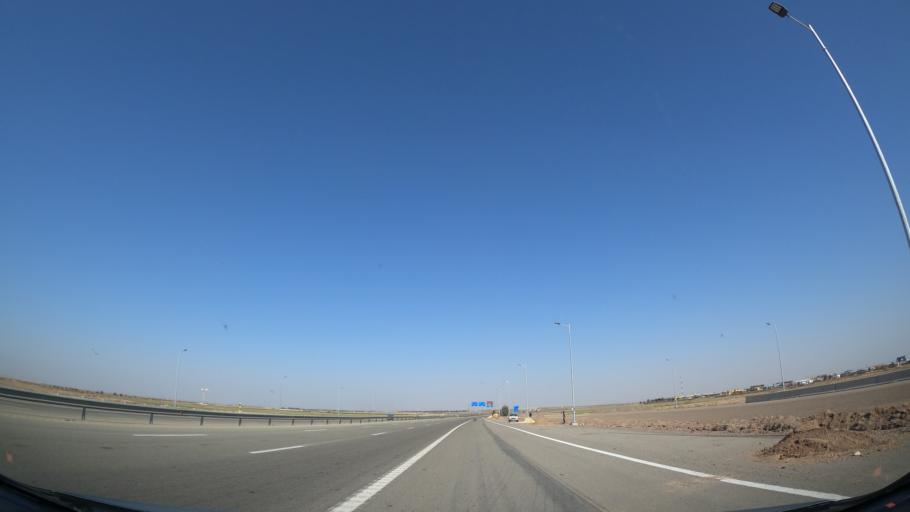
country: IR
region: Tehran
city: Eqbaliyeh
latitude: 35.1384
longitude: 51.5236
